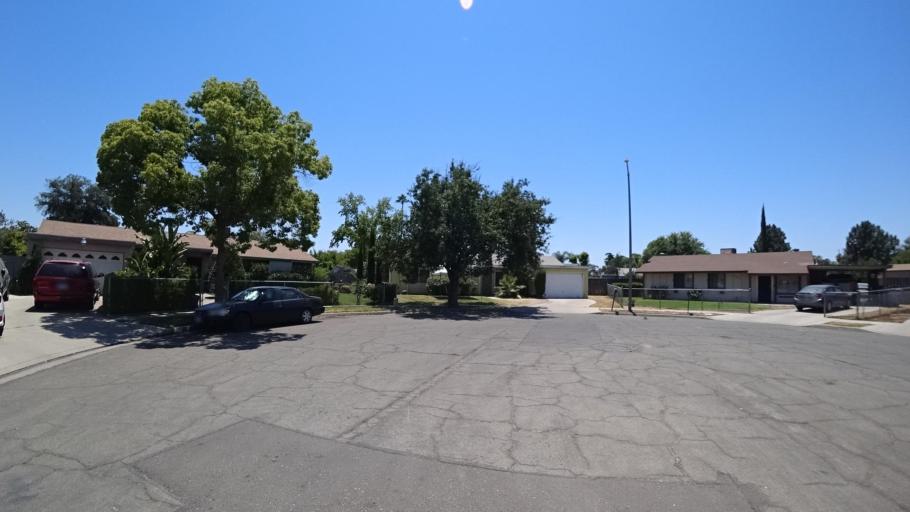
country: US
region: California
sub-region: Fresno County
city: West Park
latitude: 36.7307
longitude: -119.8334
